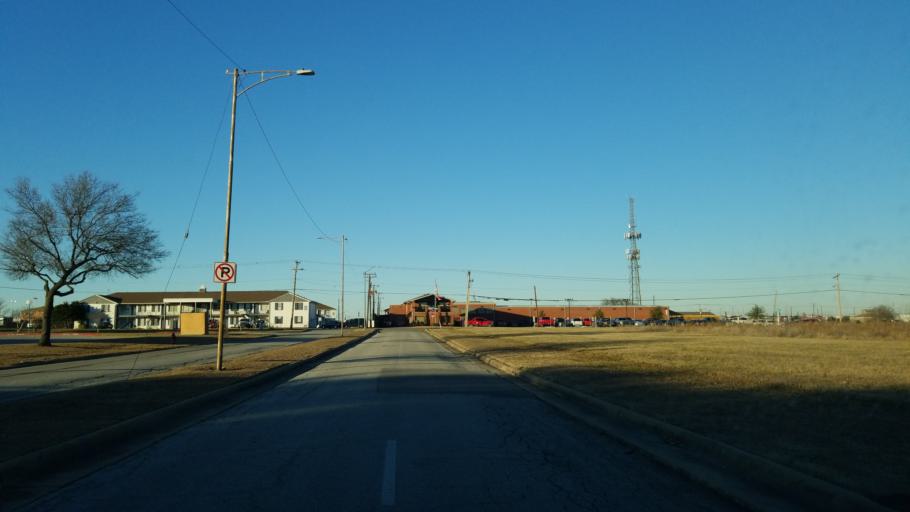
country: US
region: Texas
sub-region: Dallas County
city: Grand Prairie
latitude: 32.7341
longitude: -97.0484
